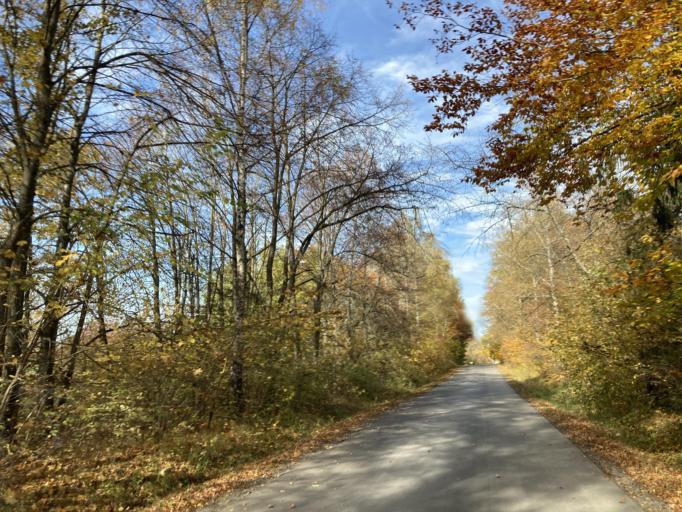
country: DE
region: Baden-Wuerttemberg
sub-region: Tuebingen Region
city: Rottenburg
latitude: 48.4554
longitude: 8.9432
